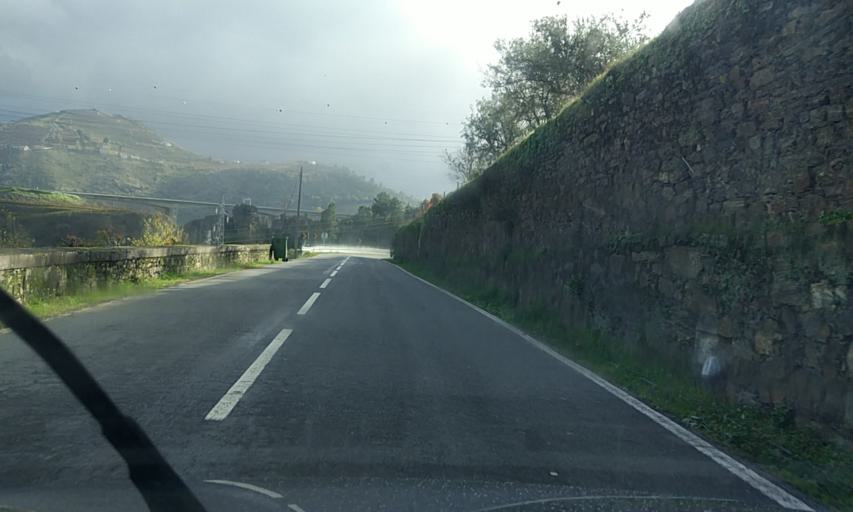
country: PT
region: Vila Real
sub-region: Peso da Regua
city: Peso da Regua
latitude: 41.1380
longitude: -7.7779
